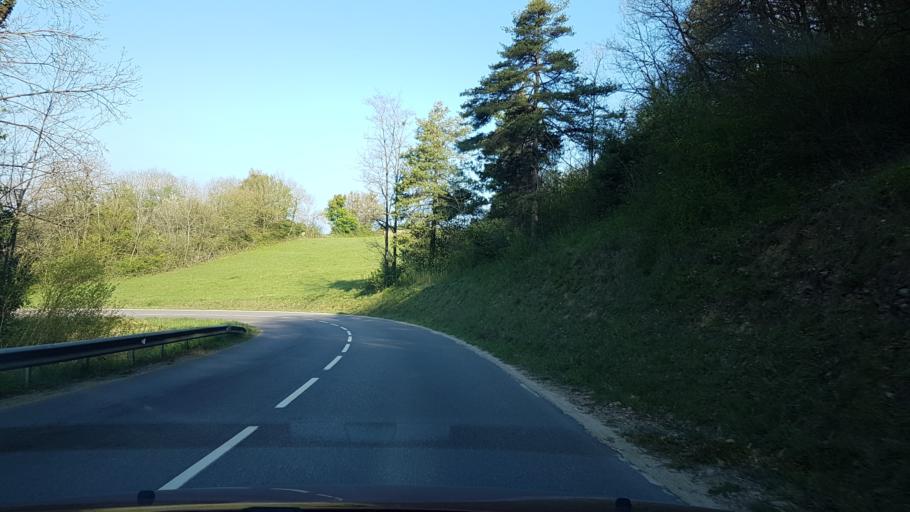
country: FR
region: Franche-Comte
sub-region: Departement du Jura
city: Saint-Amour
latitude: 46.4584
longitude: 5.3659
